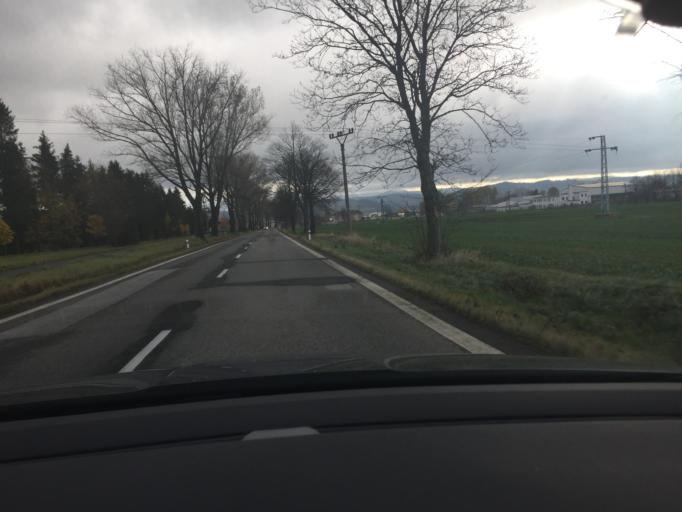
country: SK
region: Presovsky
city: Spisska Bela
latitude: 49.1966
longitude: 20.4334
